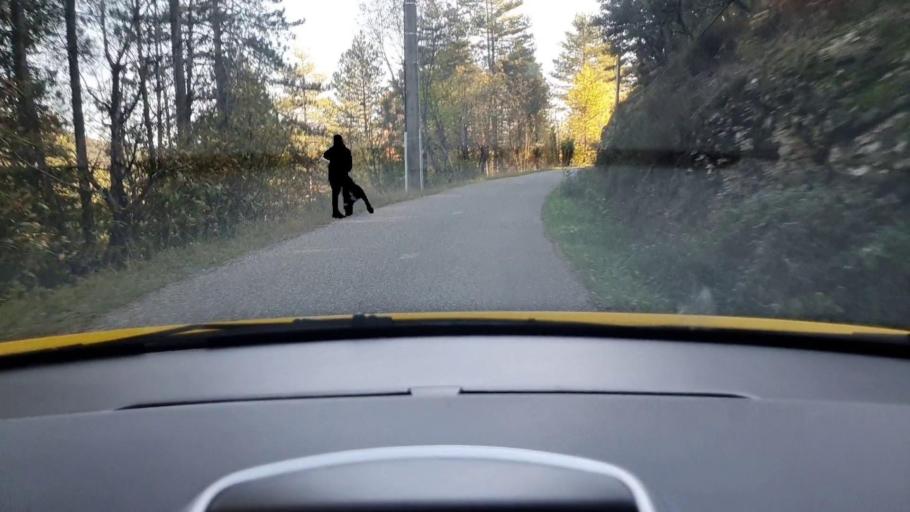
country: FR
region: Languedoc-Roussillon
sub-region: Departement du Gard
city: Sumene
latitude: 43.9786
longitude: 3.6791
